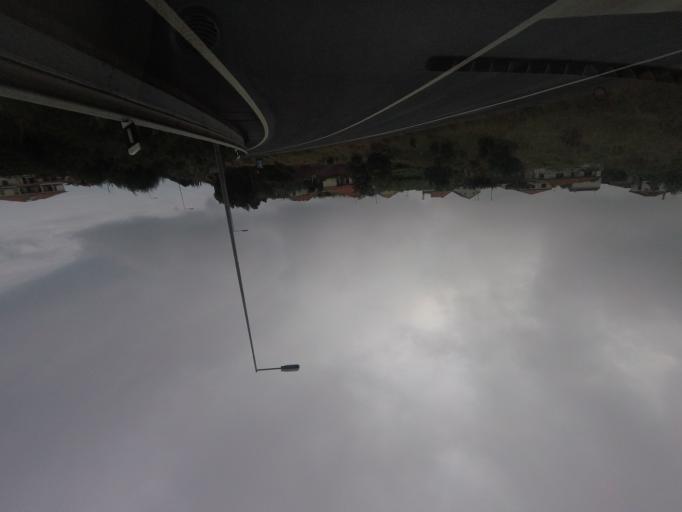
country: PT
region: Madeira
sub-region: Santana
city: Santana
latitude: 32.8113
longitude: -16.8845
